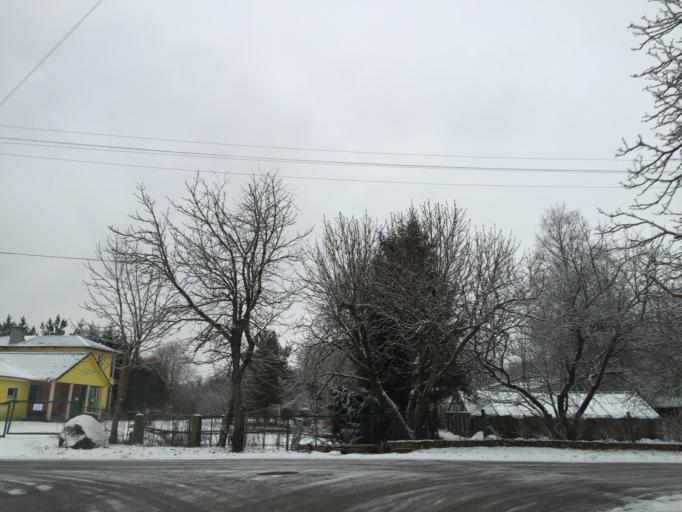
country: EE
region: Laeaene
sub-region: Lihula vald
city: Lihula
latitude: 58.6838
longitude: 23.8328
